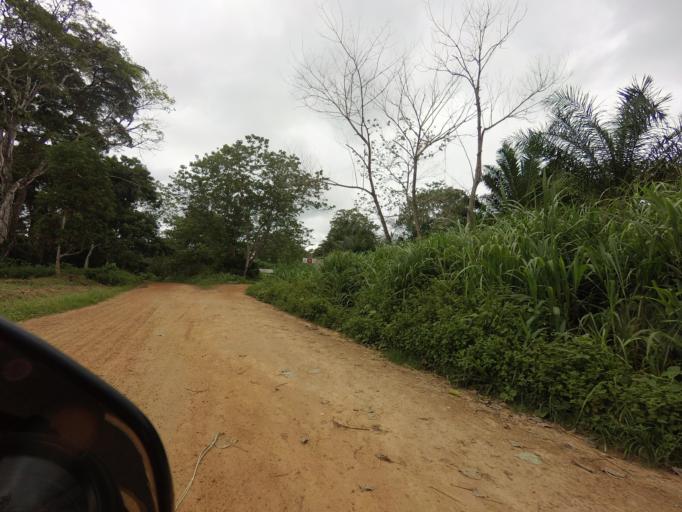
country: SL
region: Eastern Province
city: Buedu
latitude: 8.2895
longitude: -10.3701
